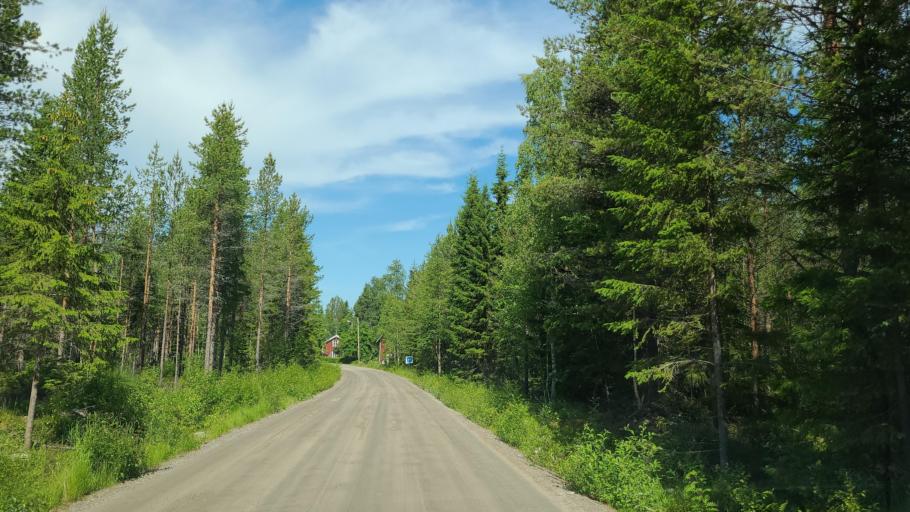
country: SE
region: Vaesterbotten
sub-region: Robertsfors Kommun
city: Robertsfors
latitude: 64.1521
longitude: 20.9507
